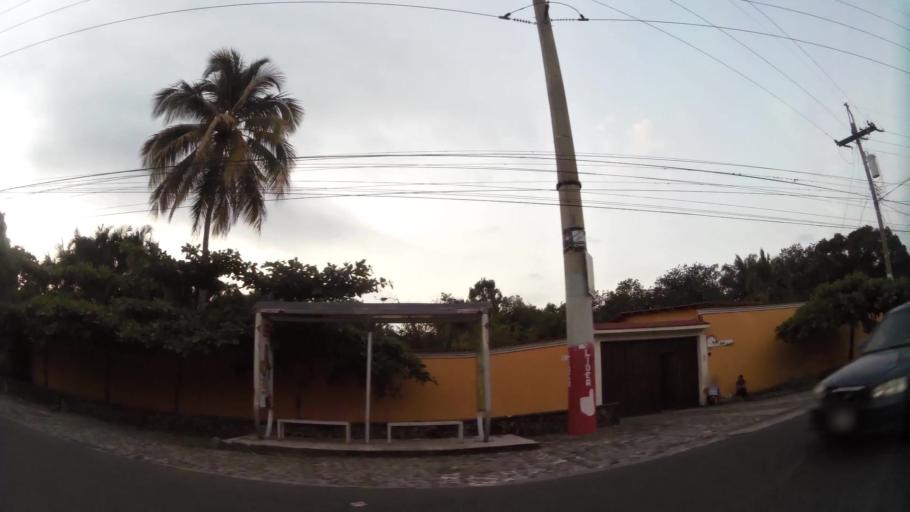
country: GT
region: Retalhuleu
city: San Martin Zapotitlan
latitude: 14.6079
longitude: -91.6077
